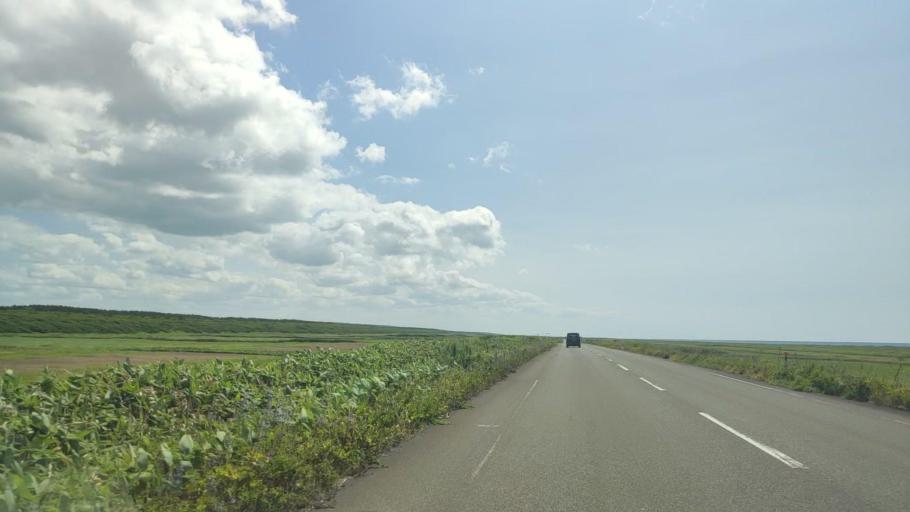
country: JP
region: Hokkaido
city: Wakkanai
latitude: 45.1493
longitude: 141.5953
